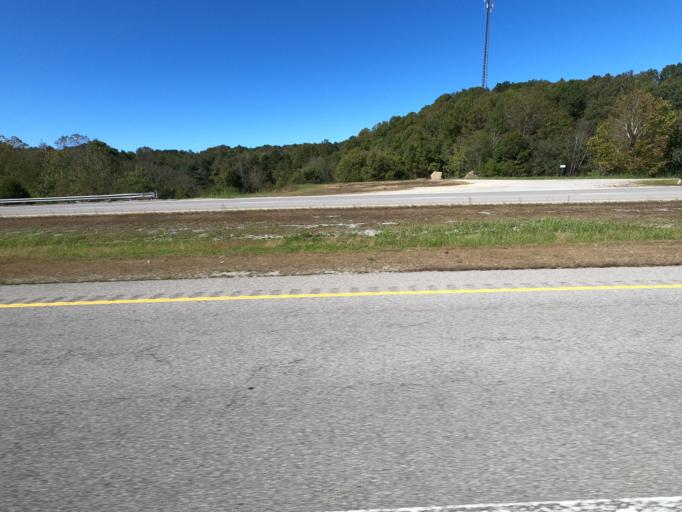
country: US
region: Tennessee
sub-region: Maury County
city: Mount Pleasant
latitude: 35.4811
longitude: -87.2564
